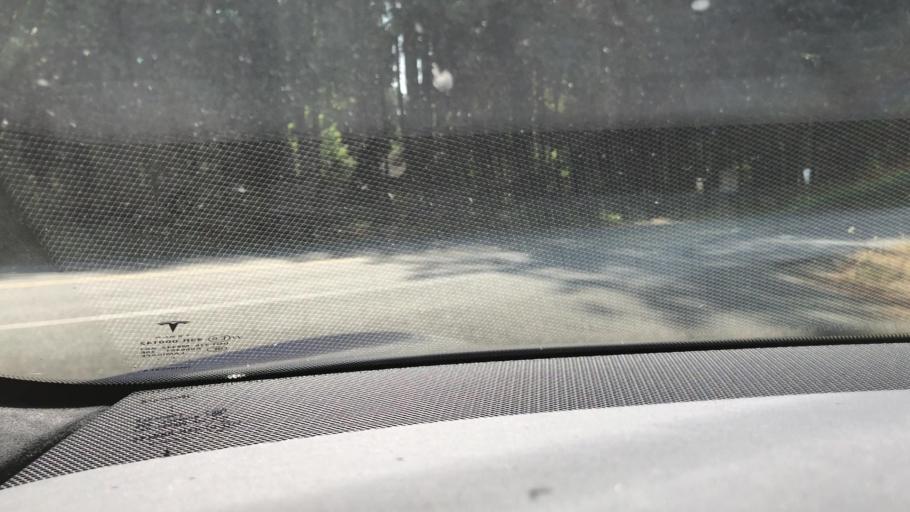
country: US
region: Washington
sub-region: Whatcom County
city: Point Roberts
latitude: 48.9975
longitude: -123.0681
